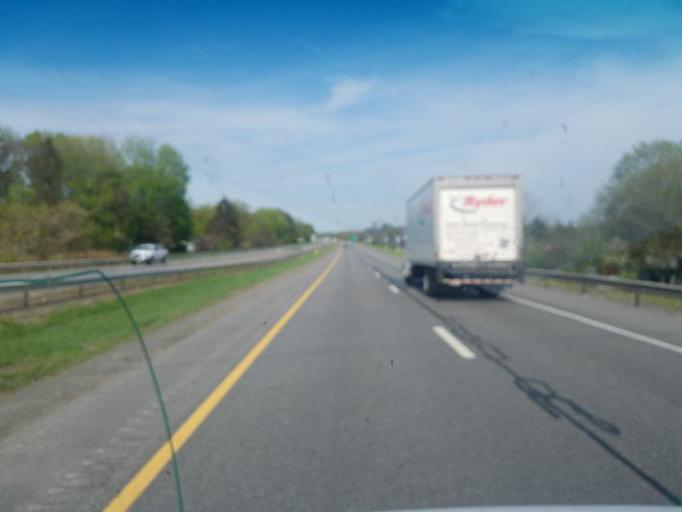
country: US
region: New York
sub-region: Onondaga County
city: Lakeland
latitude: 43.1127
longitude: -76.2577
